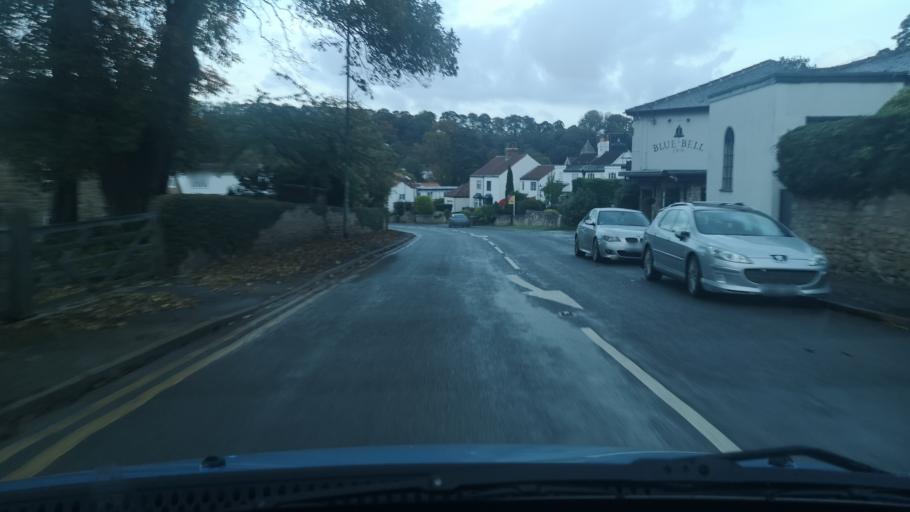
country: GB
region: England
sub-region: City and Borough of Wakefield
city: Darrington
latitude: 53.6481
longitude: -1.2639
